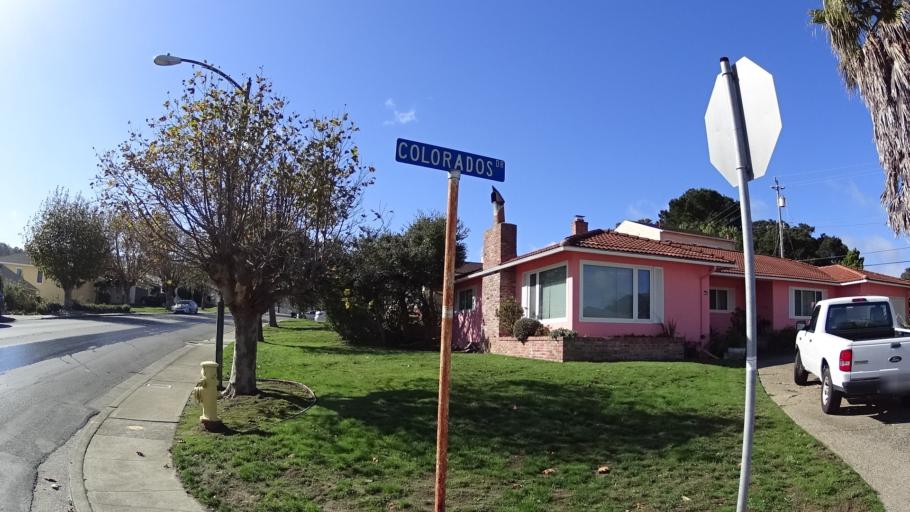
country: US
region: California
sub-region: San Mateo County
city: Millbrae
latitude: 37.5918
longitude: -122.4073
